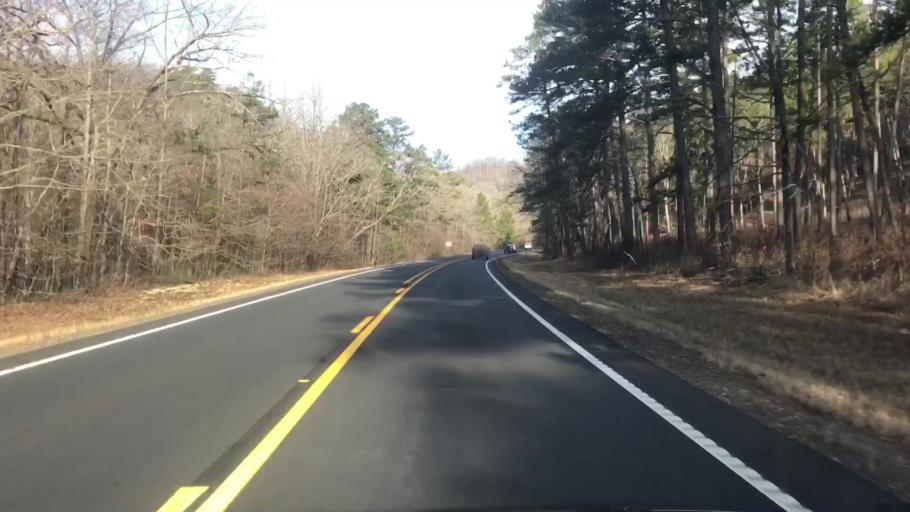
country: US
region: Arkansas
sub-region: Montgomery County
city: Mount Ida
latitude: 34.5196
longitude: -93.3886
